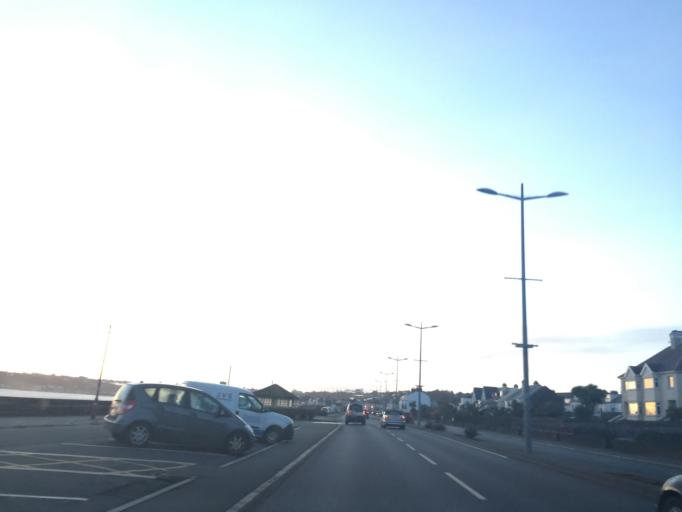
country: JE
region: St Helier
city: Saint Helier
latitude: 49.1921
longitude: -2.1250
